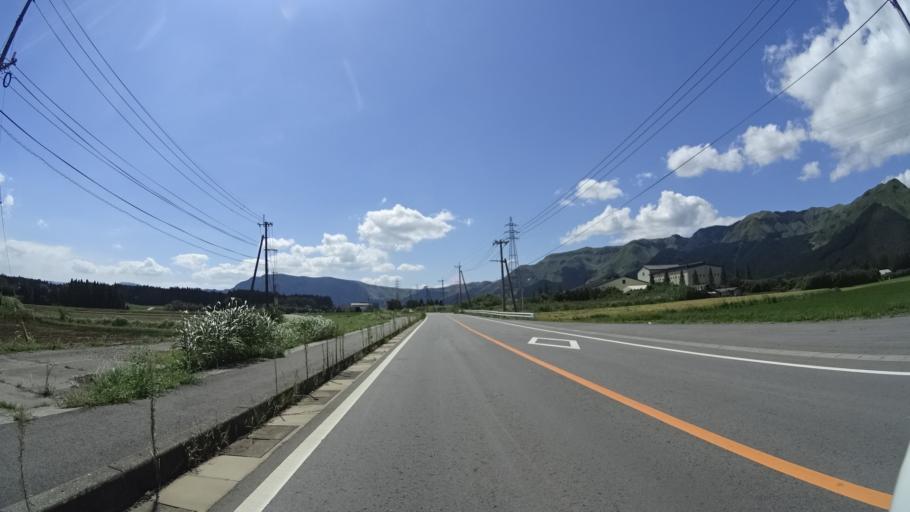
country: JP
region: Kumamoto
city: Aso
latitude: 32.9325
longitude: 131.0089
